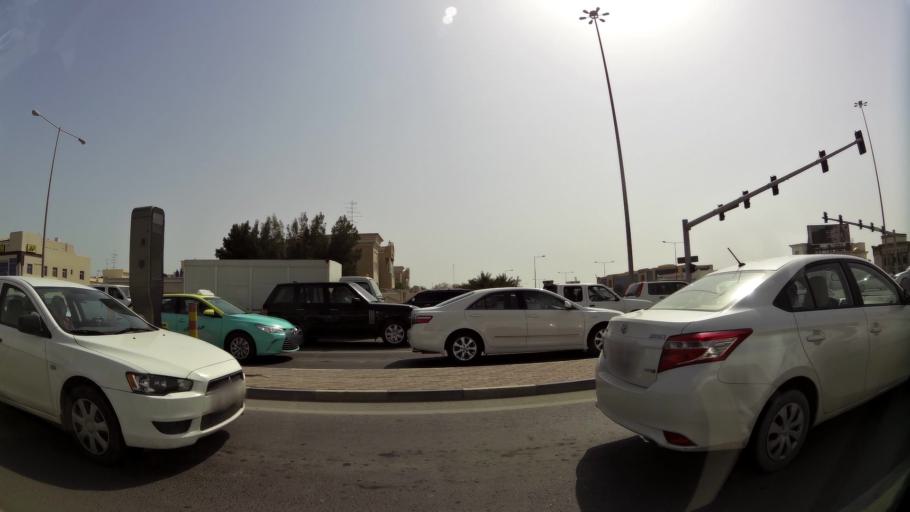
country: QA
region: Baladiyat ad Dawhah
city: Doha
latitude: 25.2547
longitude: 51.5242
